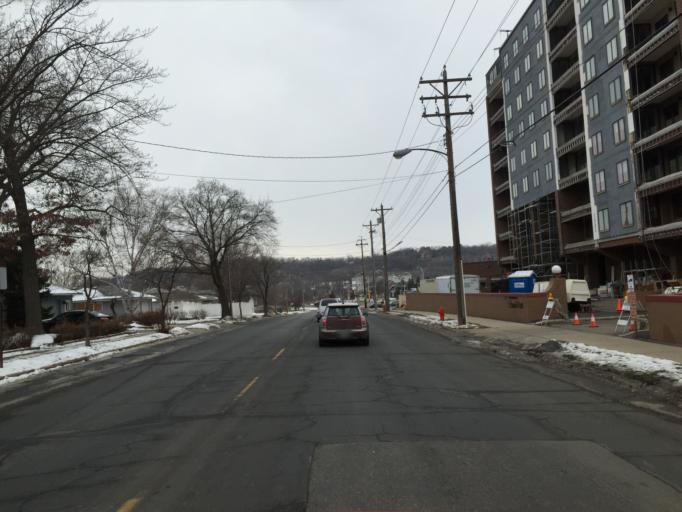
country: US
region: Minnesota
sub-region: Olmsted County
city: Rochester
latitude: 44.0368
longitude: -92.4602
